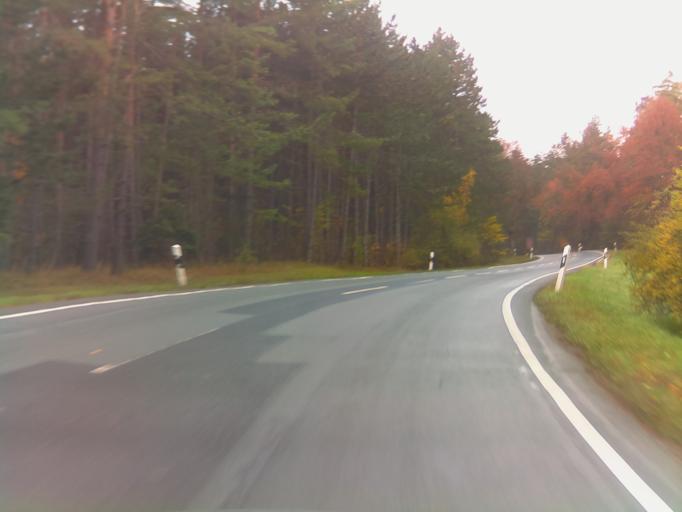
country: DE
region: Thuringia
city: Stadtilm
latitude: 50.7681
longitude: 11.0997
